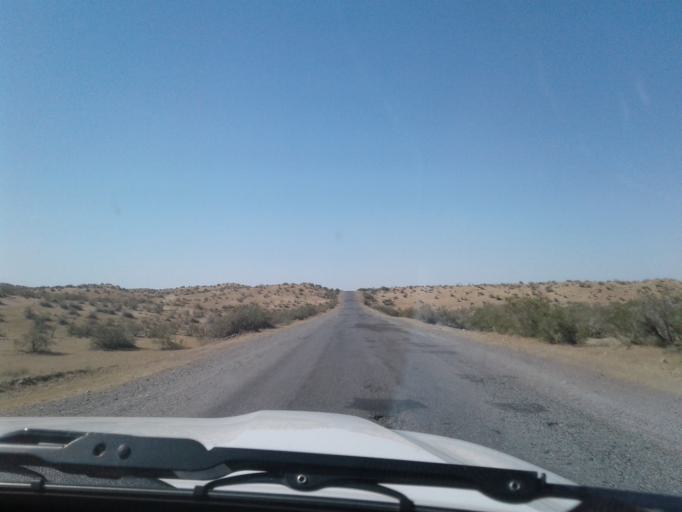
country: AF
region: Badghis
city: Bala Murghab
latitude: 36.2095
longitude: 62.6040
